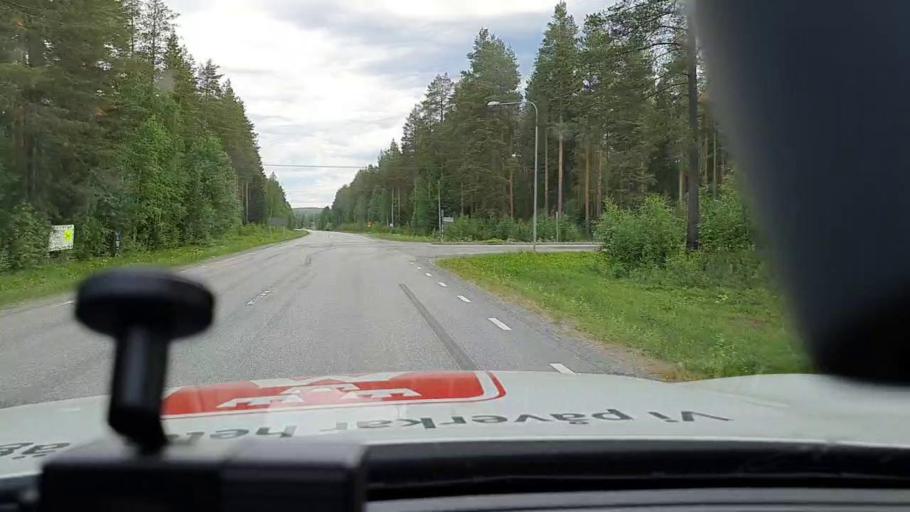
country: SE
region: Norrbotten
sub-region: Bodens Kommun
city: Boden
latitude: 65.8073
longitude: 21.6553
